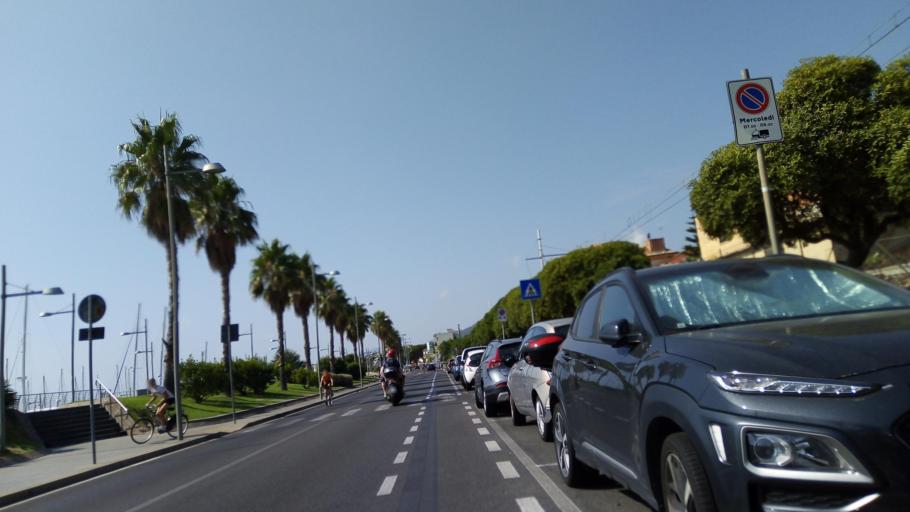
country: IT
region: Liguria
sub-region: Provincia di Savona
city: Loano
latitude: 44.1352
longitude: 8.2650
